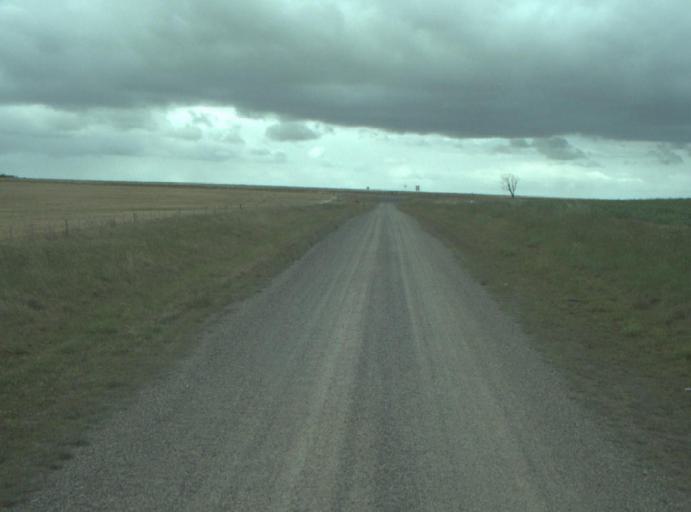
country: AU
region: Victoria
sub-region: Greater Geelong
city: Lara
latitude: -37.8895
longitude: 144.3502
